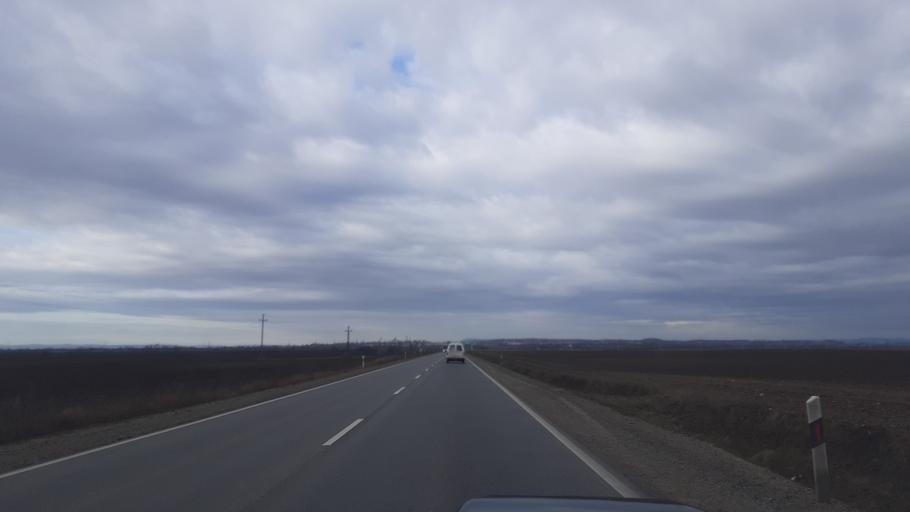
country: HU
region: Fejer
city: Pakozd
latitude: 47.1564
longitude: 18.5147
